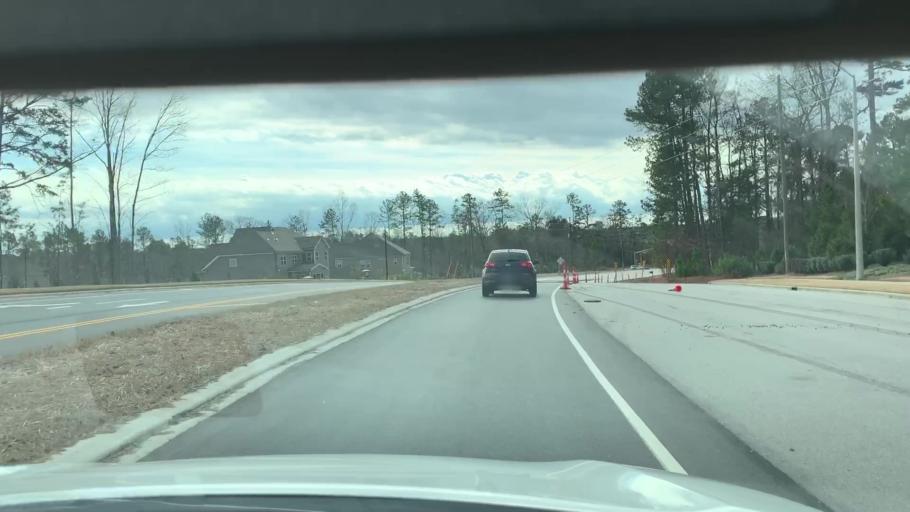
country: US
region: North Carolina
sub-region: Wake County
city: Green Level
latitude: 35.8316
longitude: -78.8992
